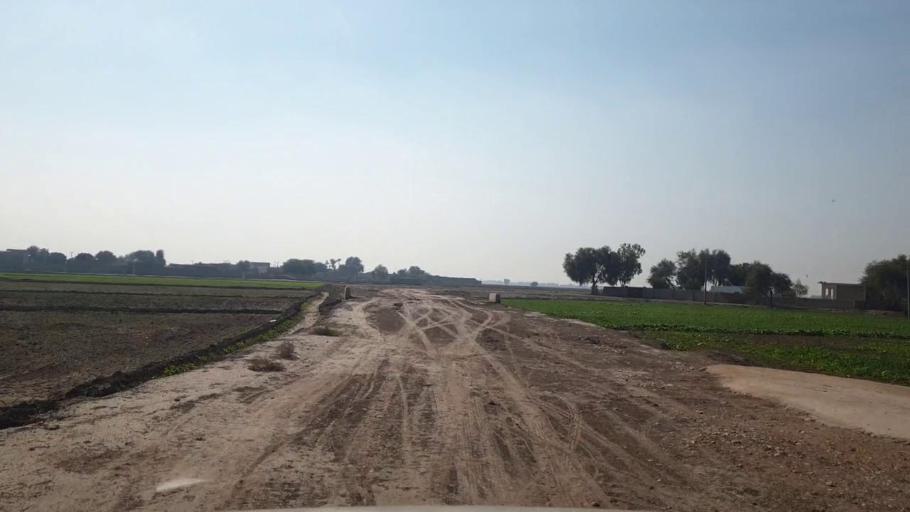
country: PK
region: Sindh
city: Bhan
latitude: 26.6491
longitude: 67.7007
